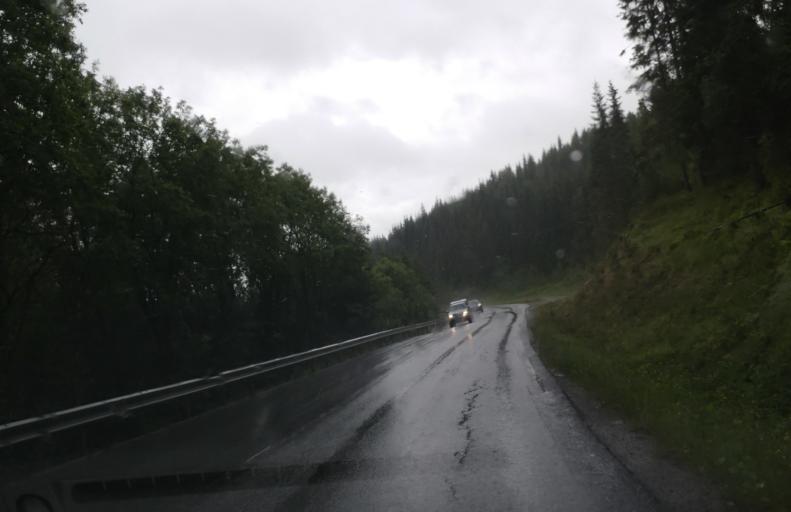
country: NO
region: Sor-Trondelag
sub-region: Selbu
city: Mebonden
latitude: 63.3070
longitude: 11.0791
